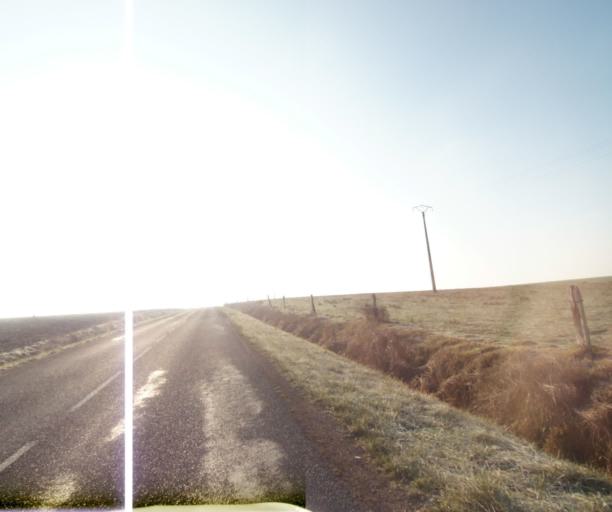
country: FR
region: Champagne-Ardenne
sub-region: Departement de la Haute-Marne
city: Montier-en-Der
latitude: 48.5022
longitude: 4.7501
